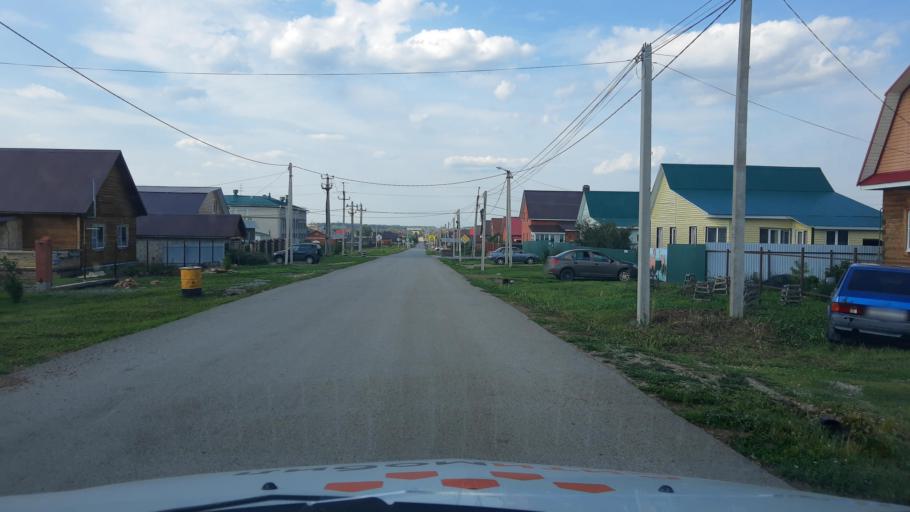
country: RU
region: Bashkortostan
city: Kabakovo
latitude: 54.6544
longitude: 56.2125
